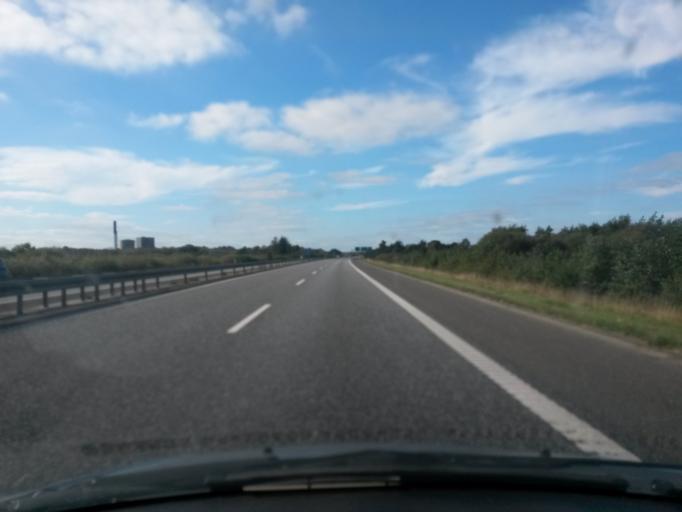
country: DK
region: Central Jutland
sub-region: Herning Kommune
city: Gjellerup Kirkeby
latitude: 56.1222
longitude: 9.0299
